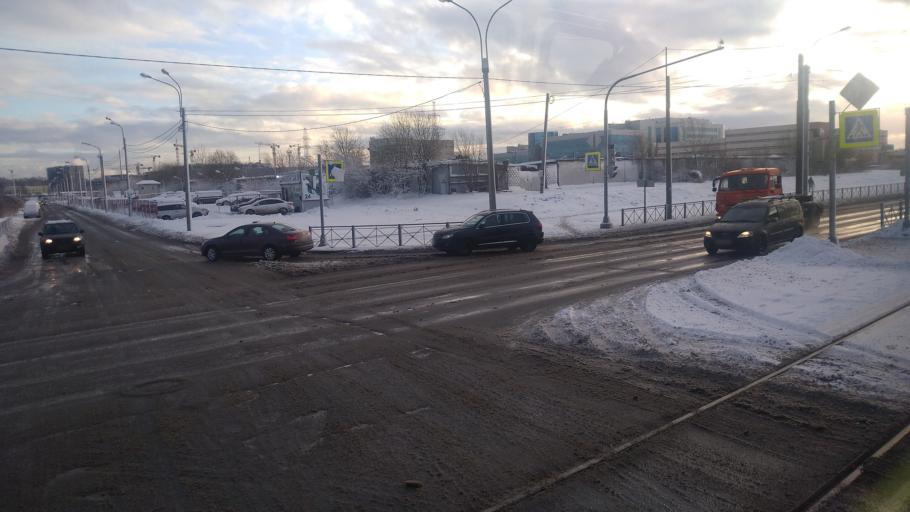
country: RU
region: St.-Petersburg
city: Staraya Derevnya
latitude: 59.9986
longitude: 30.2443
